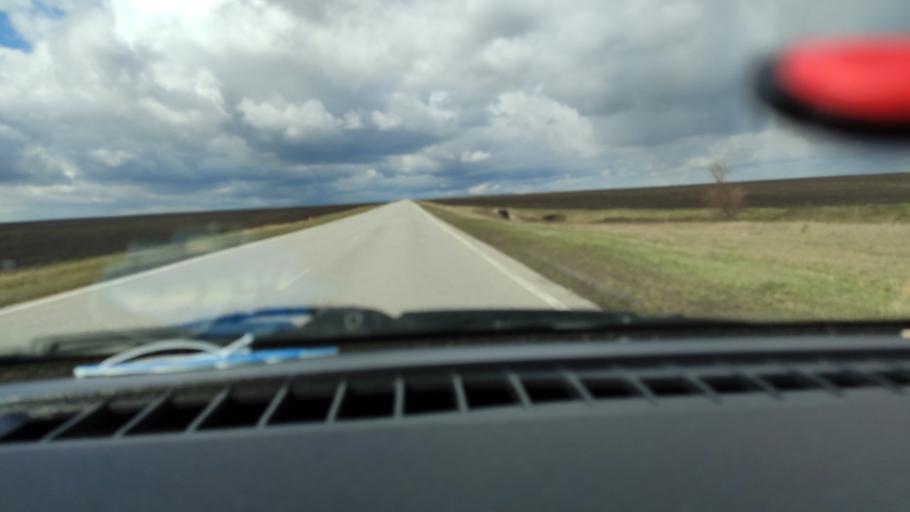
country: RU
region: Samara
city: Novyy Buyan
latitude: 53.7862
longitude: 50.0722
